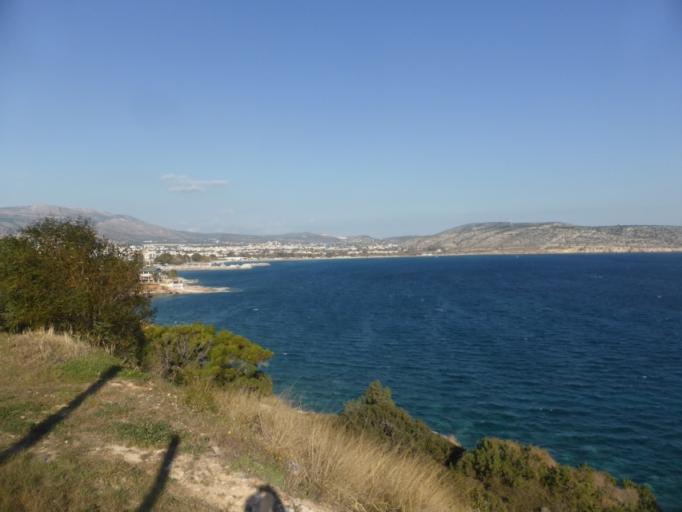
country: GR
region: Attica
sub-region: Nomarchia Anatolikis Attikis
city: Vouliagmeni
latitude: 37.8097
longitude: 23.8007
